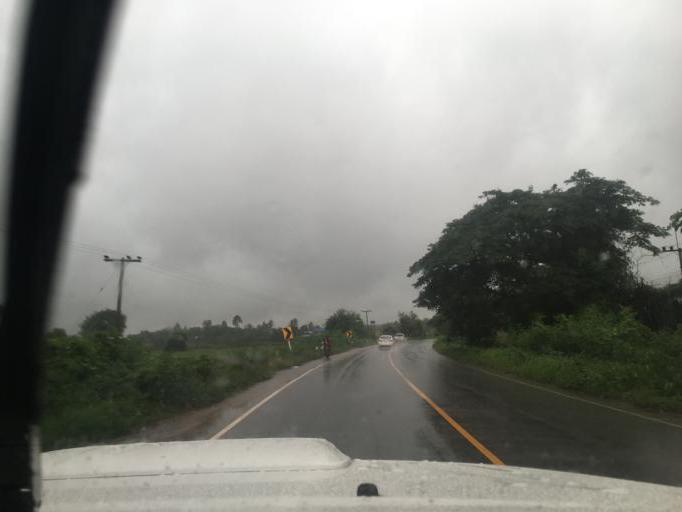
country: TH
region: Changwat Udon Thani
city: Nong Saeng
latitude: 17.2795
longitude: 102.7081
